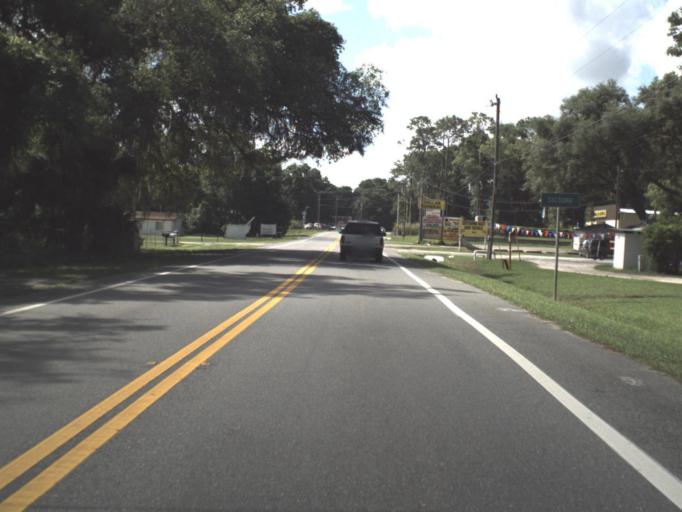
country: US
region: Florida
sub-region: Putnam County
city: Palatka
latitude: 29.5595
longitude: -81.6580
